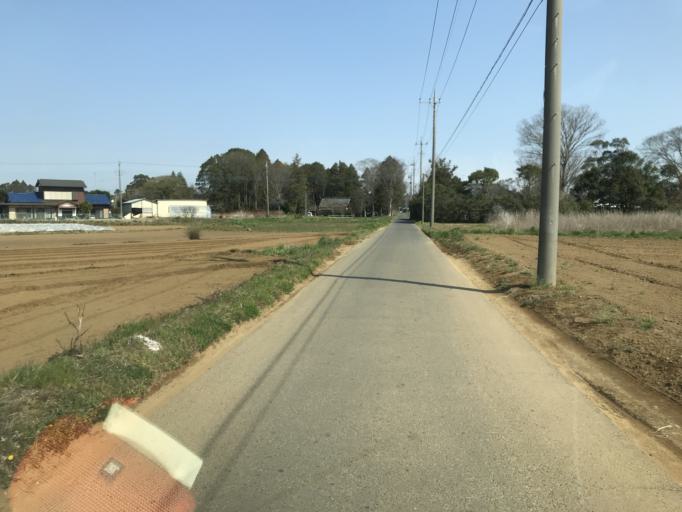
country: JP
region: Chiba
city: Sawara
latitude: 35.8362
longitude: 140.5227
